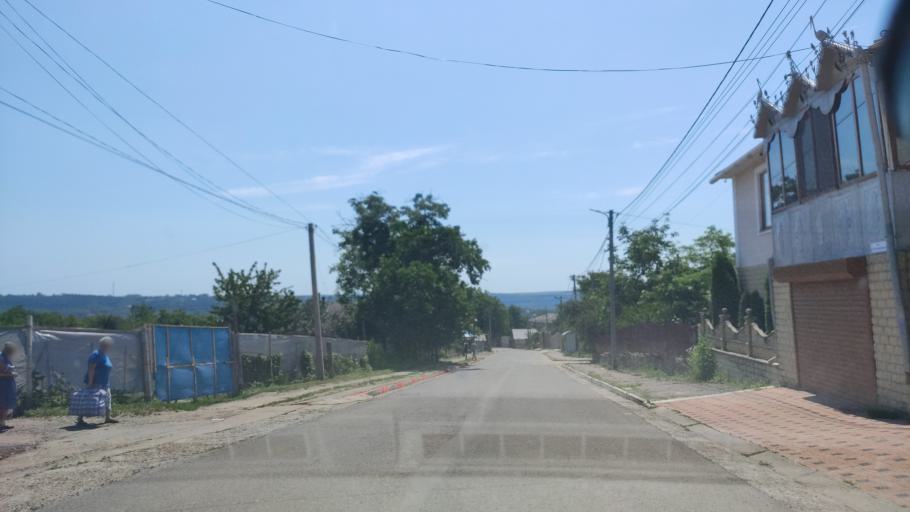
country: MD
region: Raionul Soroca
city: Soroca
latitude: 48.1700
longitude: 28.2987
